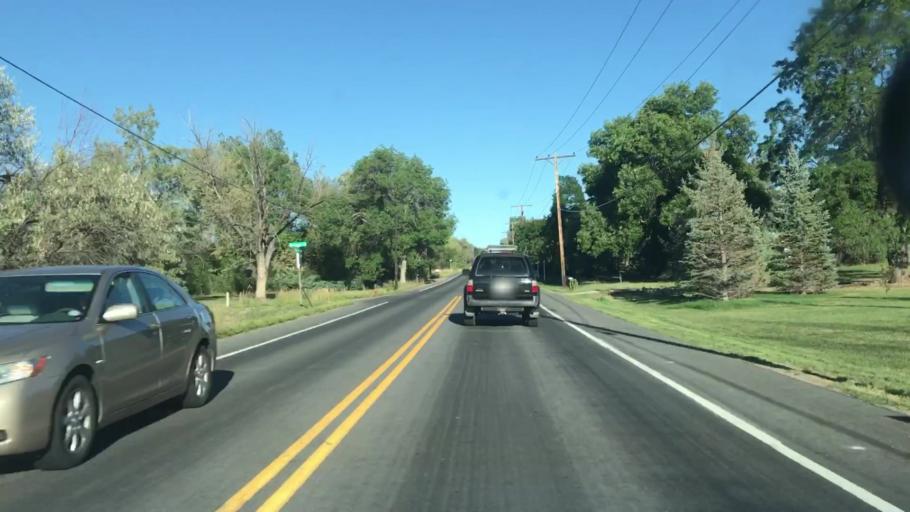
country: US
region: Colorado
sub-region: Boulder County
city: Louisville
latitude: 40.0001
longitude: -105.1701
